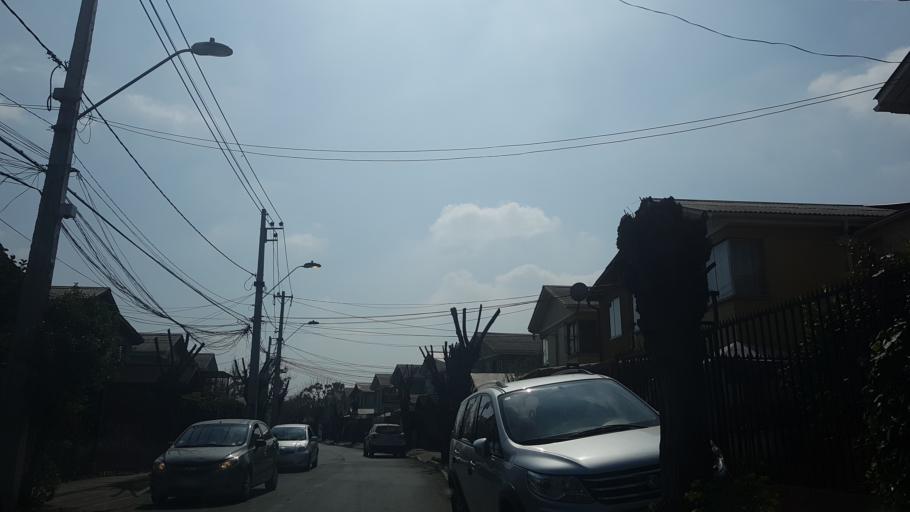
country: CL
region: Santiago Metropolitan
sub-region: Provincia de Santiago
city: Lo Prado
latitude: -33.3592
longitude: -70.7154
